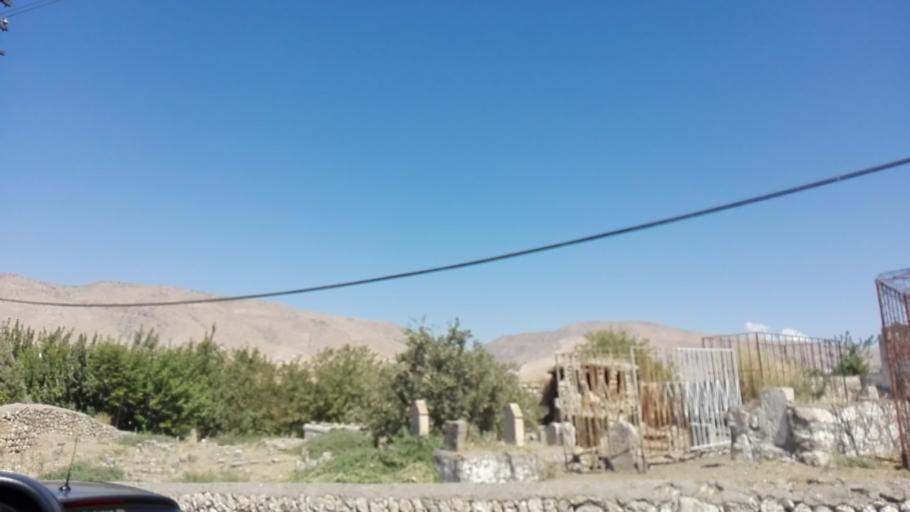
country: TR
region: Batman
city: Hasankeyf
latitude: 37.7133
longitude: 41.4140
